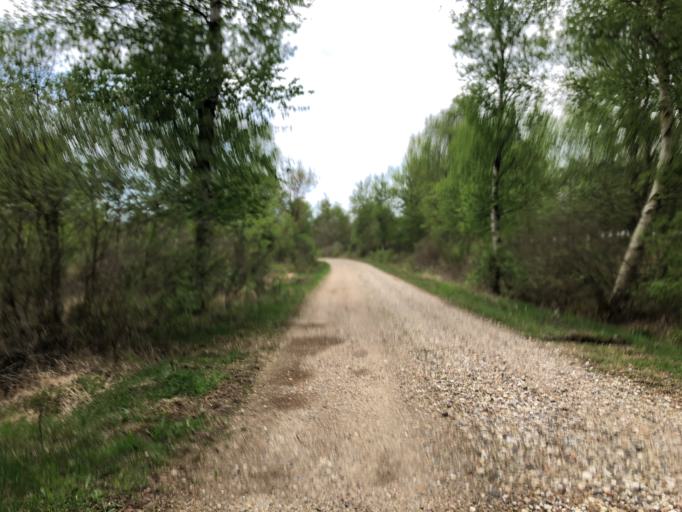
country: DK
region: Central Jutland
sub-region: Holstebro Kommune
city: Ulfborg
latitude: 56.2784
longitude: 8.4335
